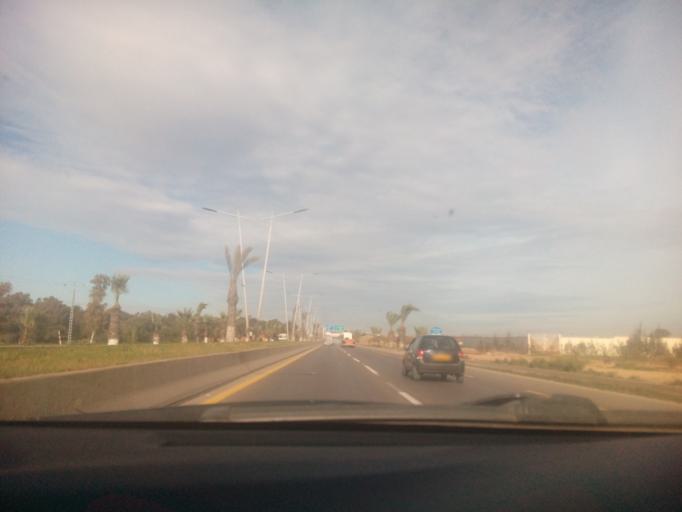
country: DZ
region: Oran
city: Es Senia
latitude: 35.6613
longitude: -0.5932
